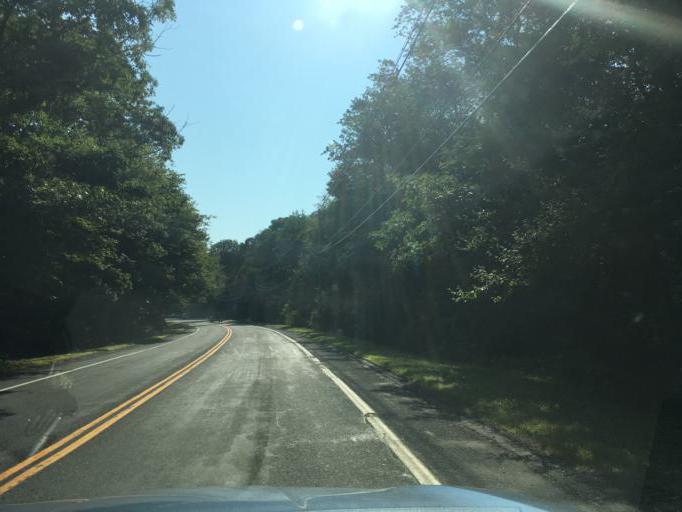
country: US
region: Rhode Island
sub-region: Washington County
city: Kingston
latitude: 41.4827
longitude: -71.5031
